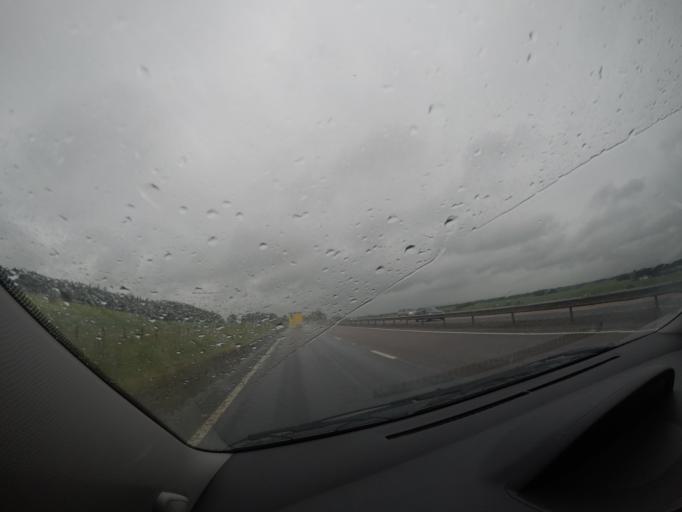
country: GB
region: Scotland
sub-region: Angus
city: Forfar
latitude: 56.6779
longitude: -2.8790
